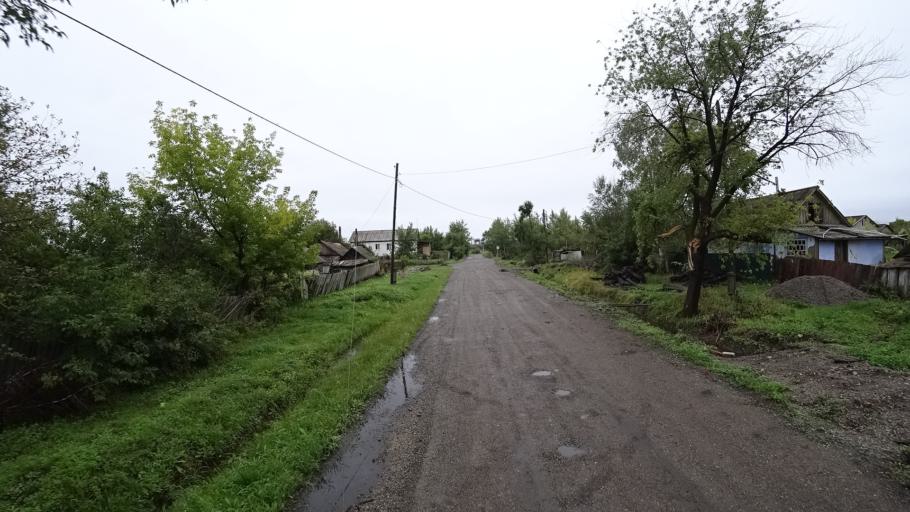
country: RU
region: Primorskiy
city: Monastyrishche
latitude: 44.2106
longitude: 132.4359
